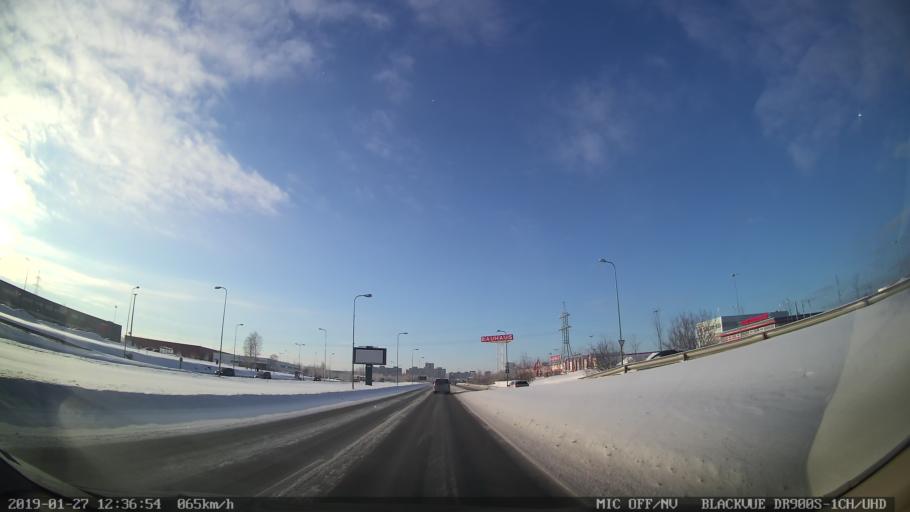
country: EE
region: Harju
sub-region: Tallinna linn
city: Kose
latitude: 59.4419
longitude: 24.8636
